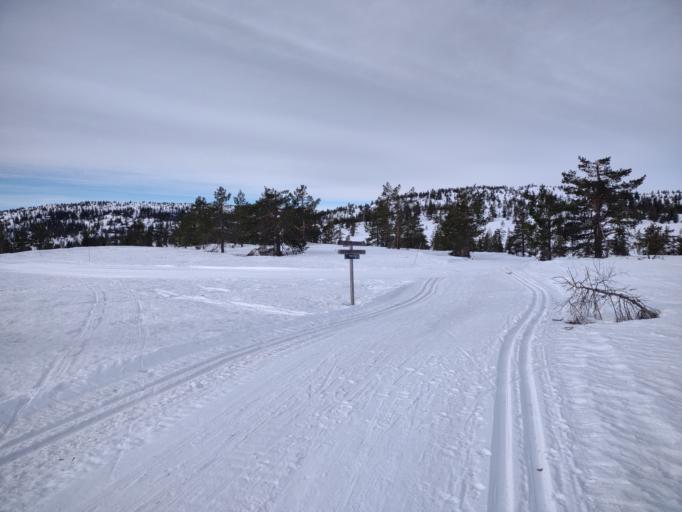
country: NO
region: Buskerud
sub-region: Flesberg
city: Lampeland
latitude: 59.7601
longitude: 9.4447
